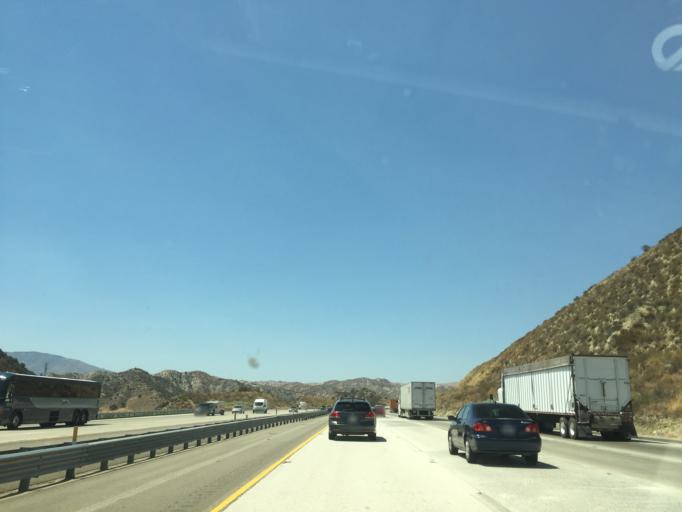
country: US
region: California
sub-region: Kern County
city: Lebec
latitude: 34.6958
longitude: -118.7911
